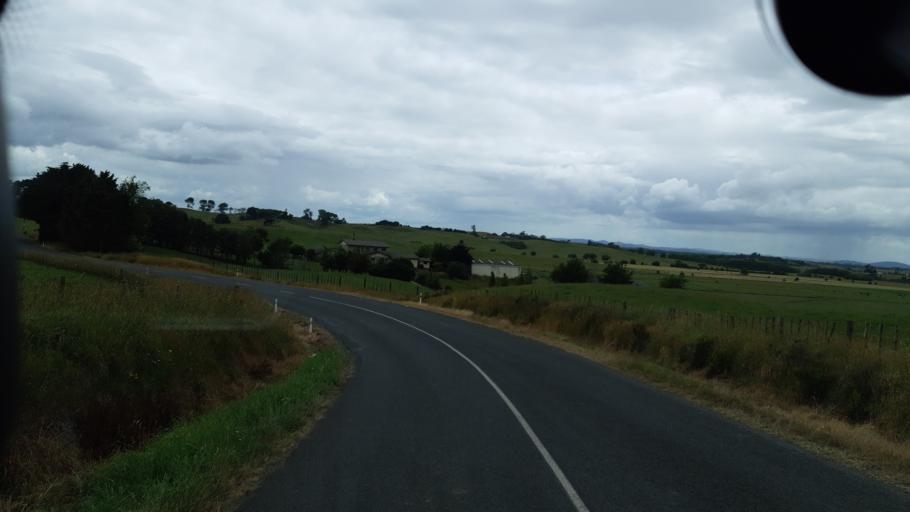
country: NZ
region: Waikato
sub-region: Waikato District
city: Te Kauwhata
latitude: -37.5029
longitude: 175.0899
